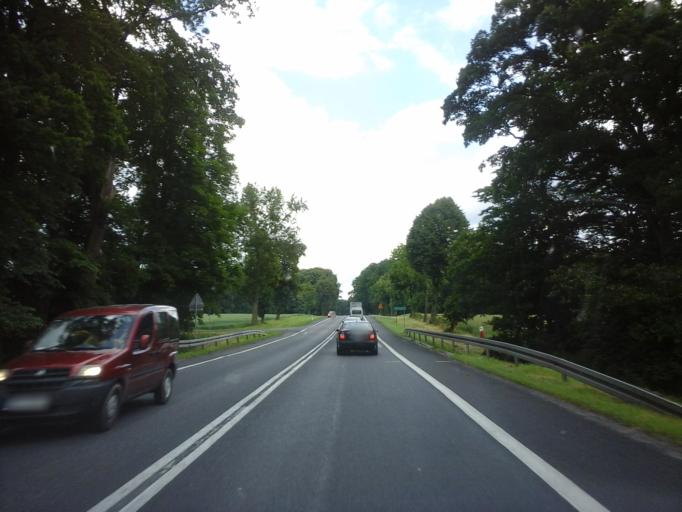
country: PL
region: West Pomeranian Voivodeship
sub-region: Powiat bialogardzki
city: Bialogard
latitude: 54.0985
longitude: 15.9942
